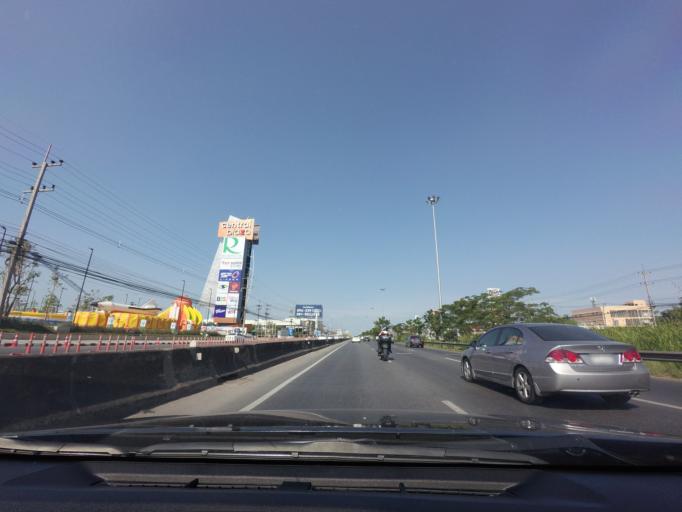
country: TH
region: Samut Sakhon
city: Samut Sakhon
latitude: 13.5711
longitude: 100.2900
